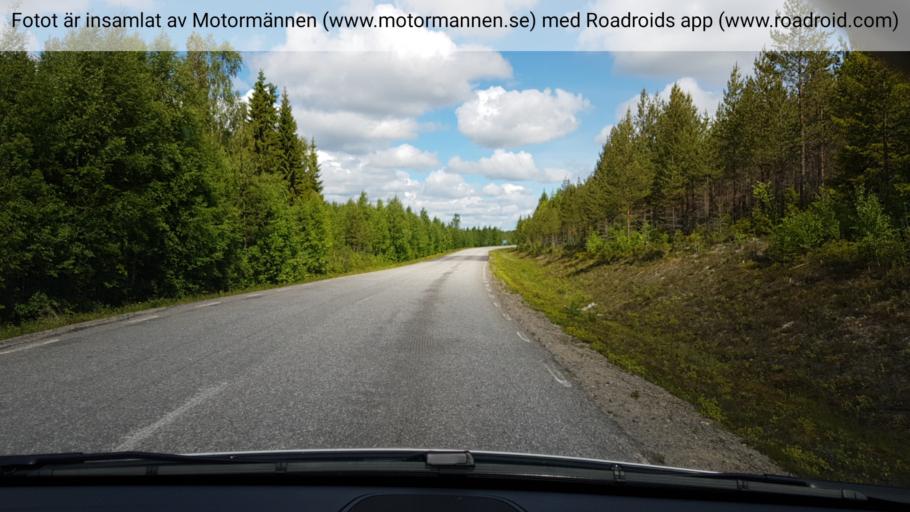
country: SE
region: Vaesterbotten
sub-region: Vannas Kommun
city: Vannasby
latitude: 64.0378
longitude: 19.9311
